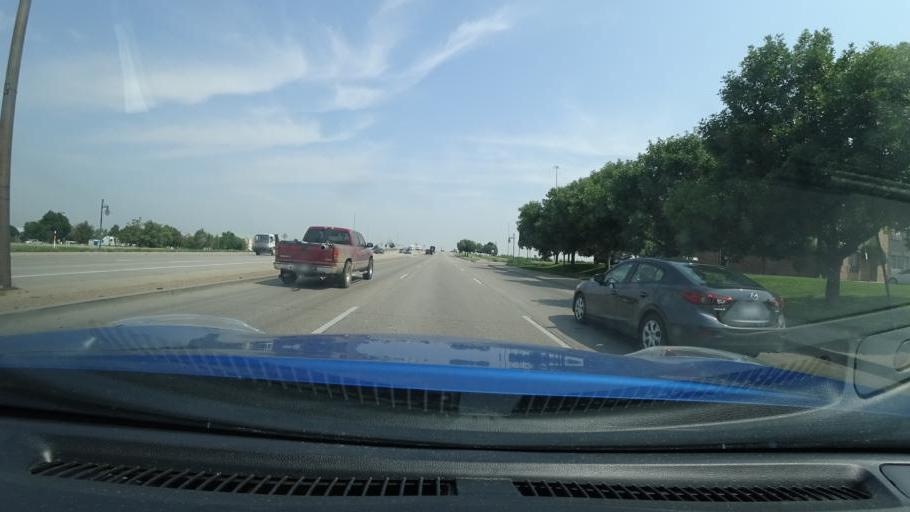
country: US
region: Colorado
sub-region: Adams County
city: Aurora
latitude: 39.7625
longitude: -104.7910
